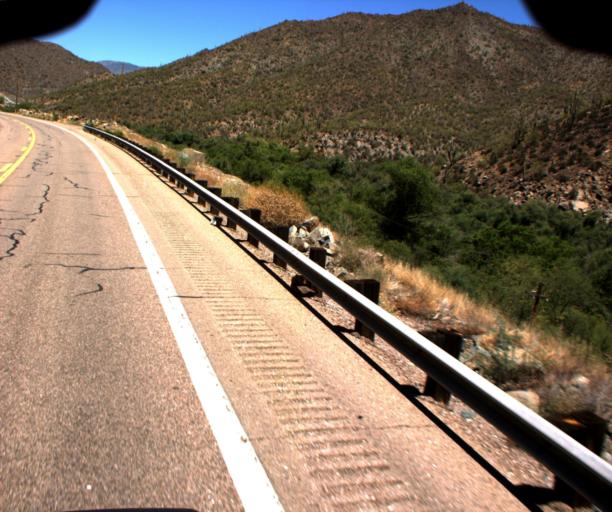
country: US
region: Arizona
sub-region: Pinal County
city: Kearny
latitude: 33.0563
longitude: -110.7193
